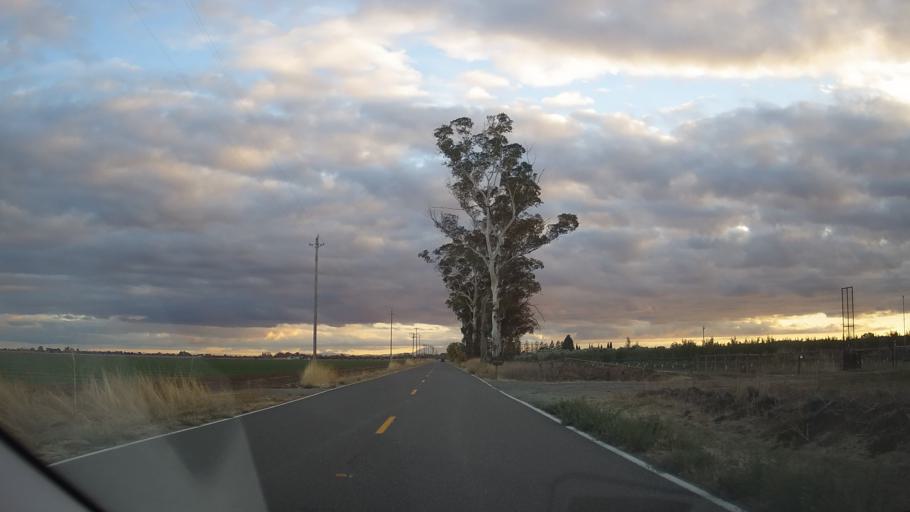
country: US
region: California
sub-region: Solano County
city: Hartley
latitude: 38.3807
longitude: -121.9059
